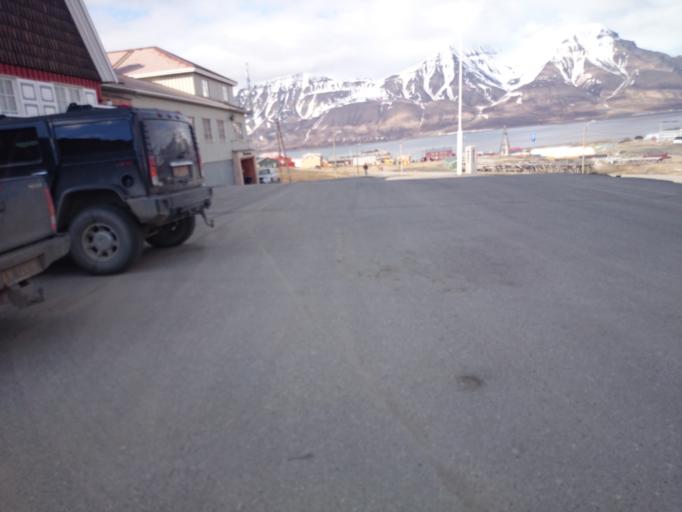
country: SJ
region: Svalbard
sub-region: Spitsbergen
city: Longyearbyen
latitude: 78.2194
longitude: 15.6182
